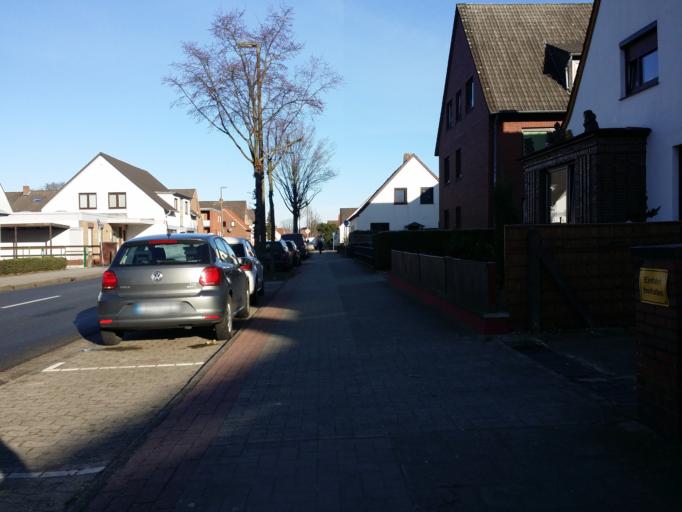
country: DE
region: Lower Saxony
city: Delmenhorst
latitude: 53.0382
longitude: 8.6502
